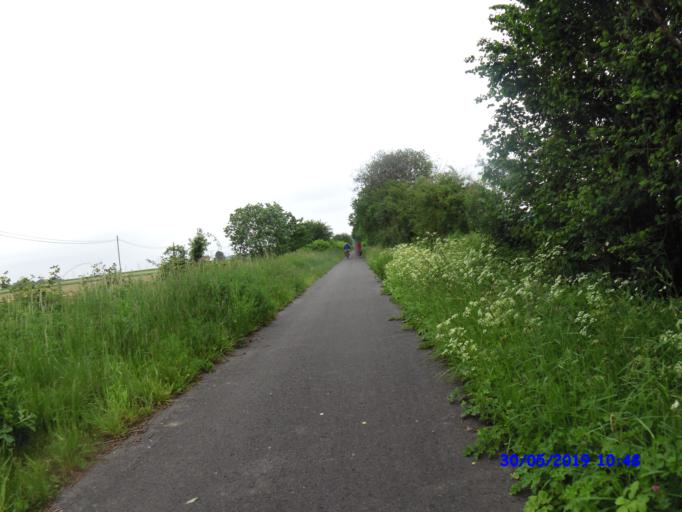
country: BE
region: Wallonia
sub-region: Province du Hainaut
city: Beaumont
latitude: 50.2540
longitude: 4.2703
